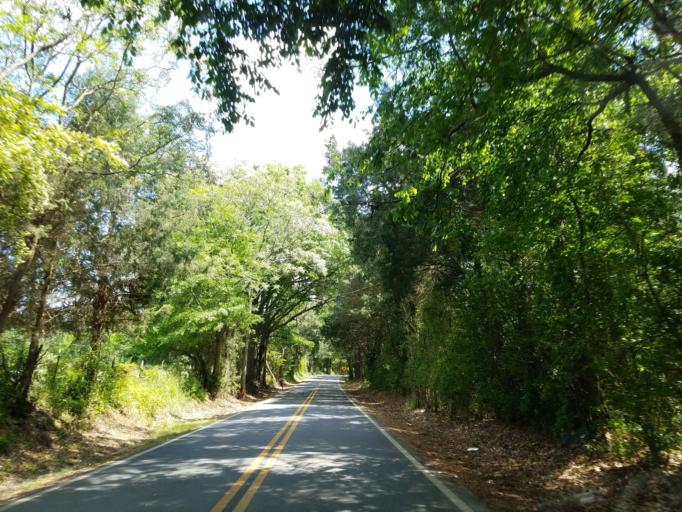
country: US
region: Georgia
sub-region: Monroe County
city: Forsyth
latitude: 33.0818
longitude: -83.9549
